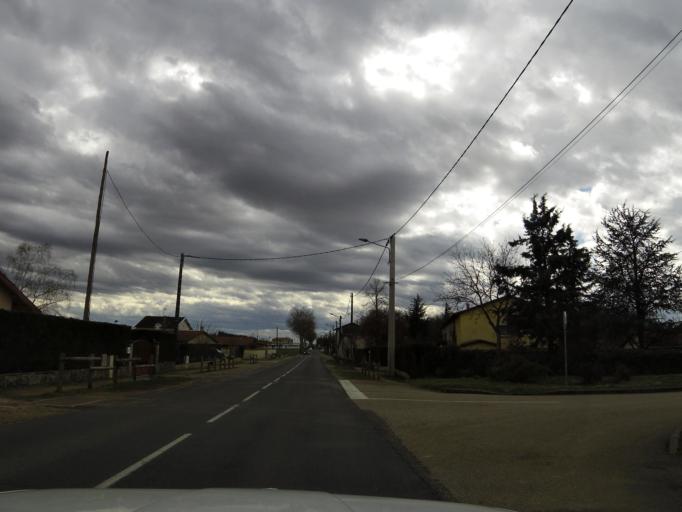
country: FR
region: Rhone-Alpes
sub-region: Departement de l'Ain
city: Meximieux
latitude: 45.9176
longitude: 5.2207
